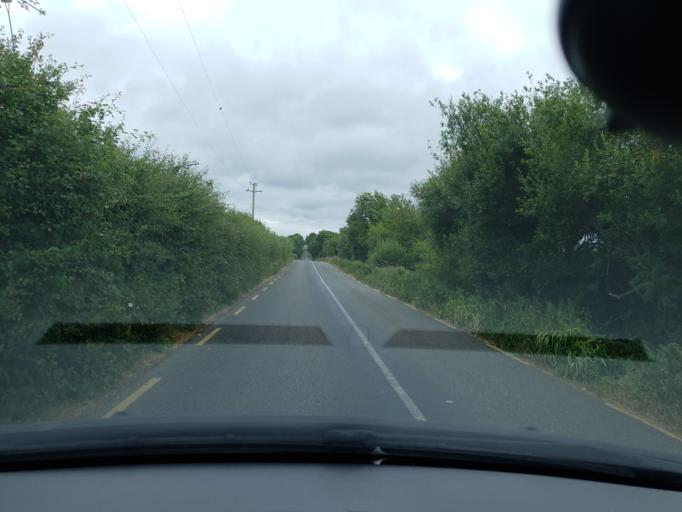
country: IE
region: Munster
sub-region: Ciarrai
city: Cill Airne
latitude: 52.1631
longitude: -9.6053
